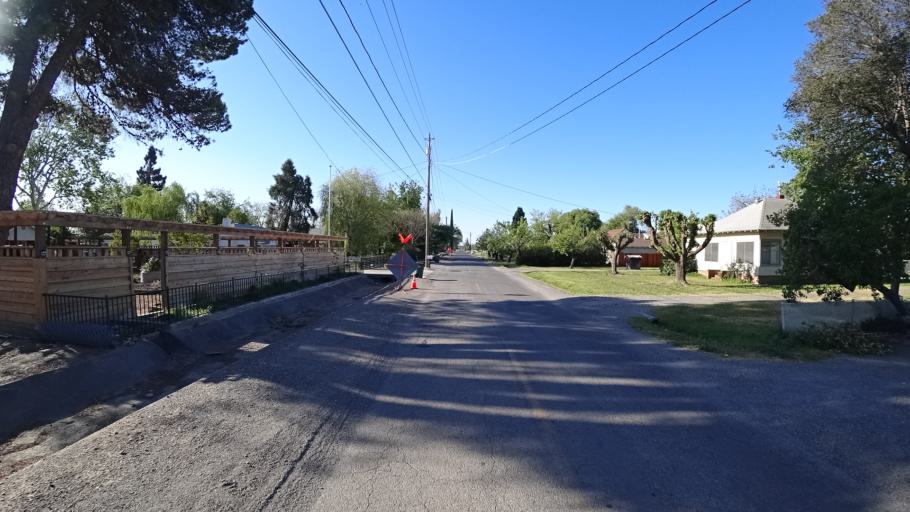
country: US
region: California
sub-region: Glenn County
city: Orland
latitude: 39.7376
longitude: -122.1875
